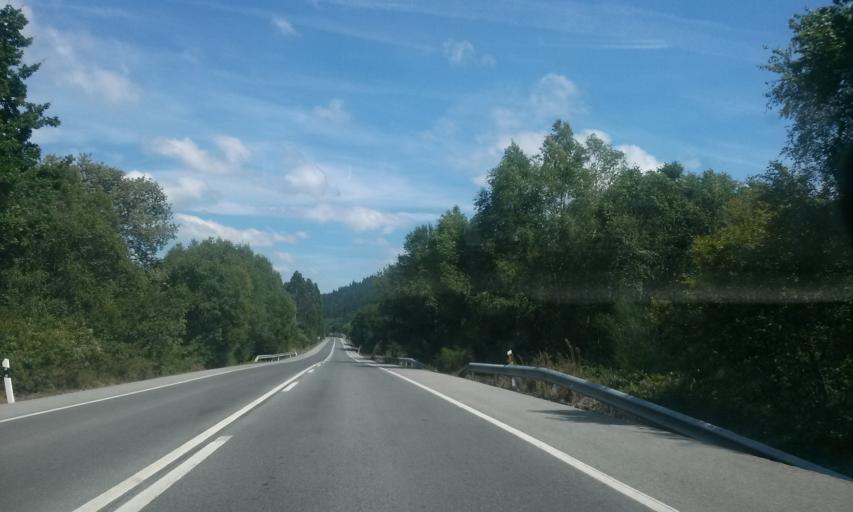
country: ES
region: Galicia
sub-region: Provincia de Lugo
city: Guitiriz
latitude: 43.1750
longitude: -7.8021
